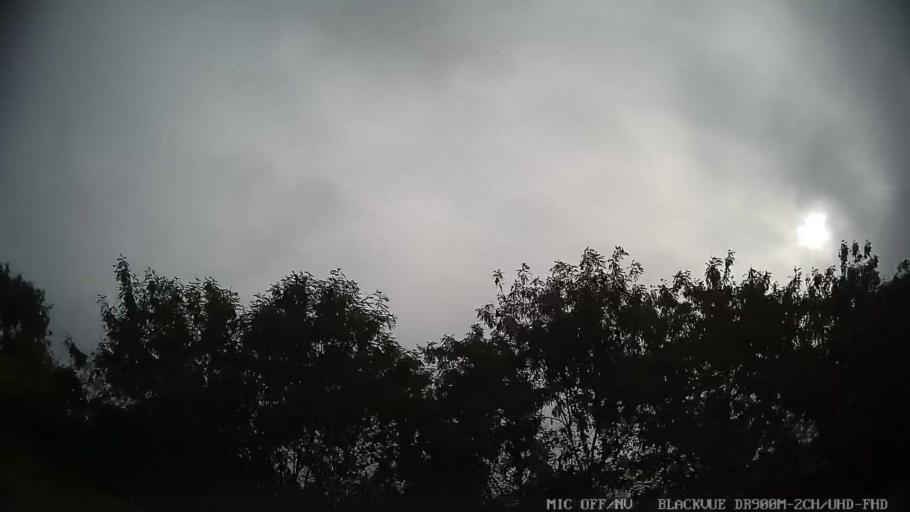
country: BR
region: Sao Paulo
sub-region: Osasco
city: Osasco
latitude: -23.4818
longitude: -46.7318
